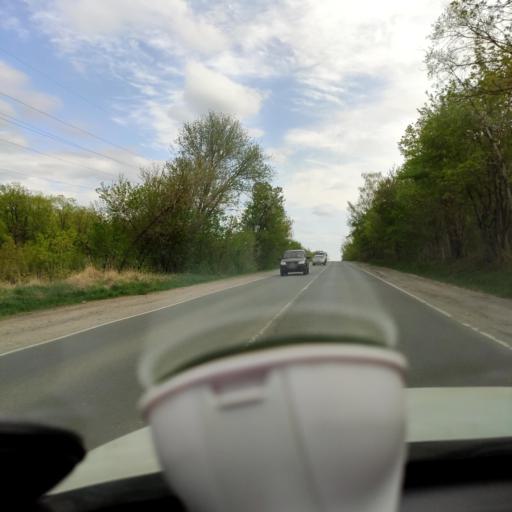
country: RU
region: Samara
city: Novosemeykino
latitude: 53.3196
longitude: 50.2672
